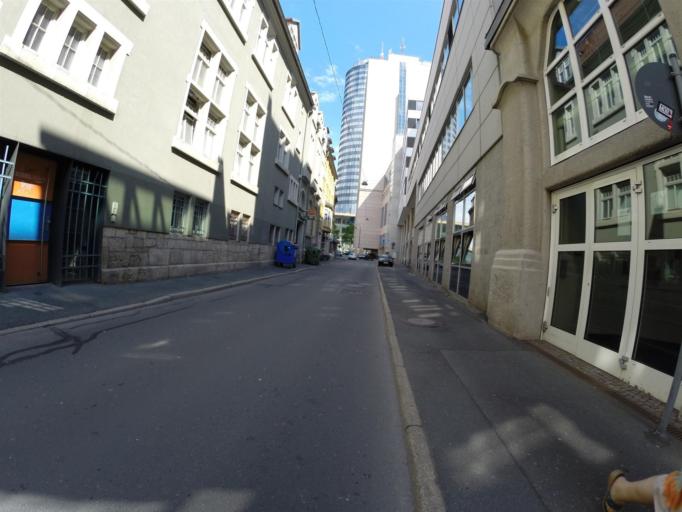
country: DE
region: Thuringia
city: Jena
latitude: 50.9292
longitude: 11.5820
